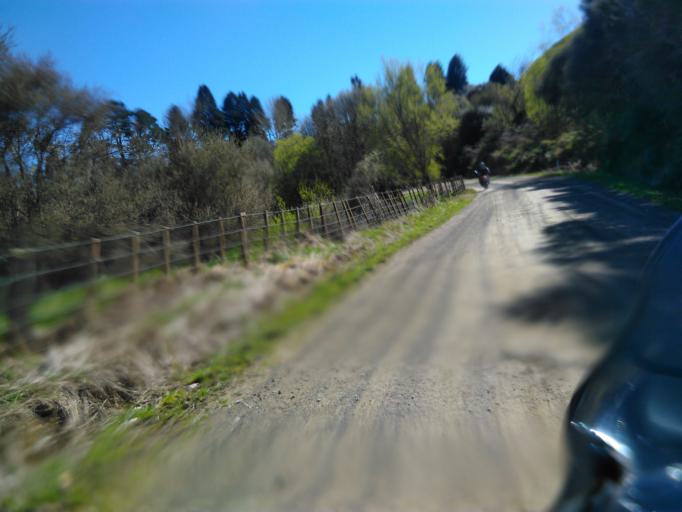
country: NZ
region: Bay of Plenty
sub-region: Opotiki District
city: Opotiki
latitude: -38.2962
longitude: 177.5524
